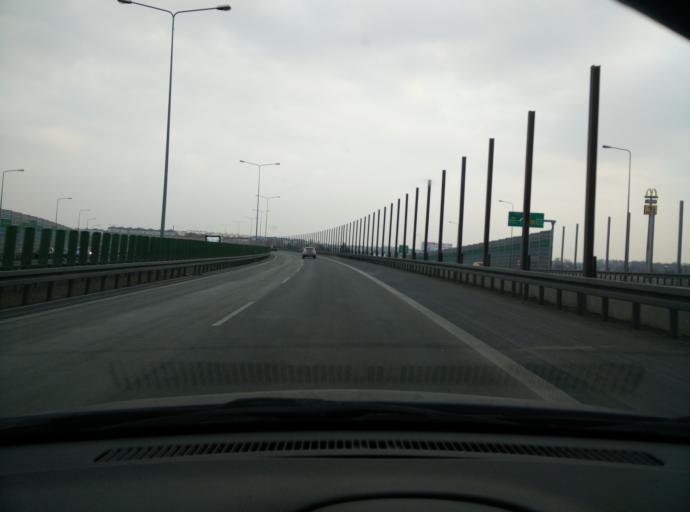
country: PL
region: Greater Poland Voivodeship
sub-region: Powiat poznanski
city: Kornik
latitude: 52.2590
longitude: 17.0765
